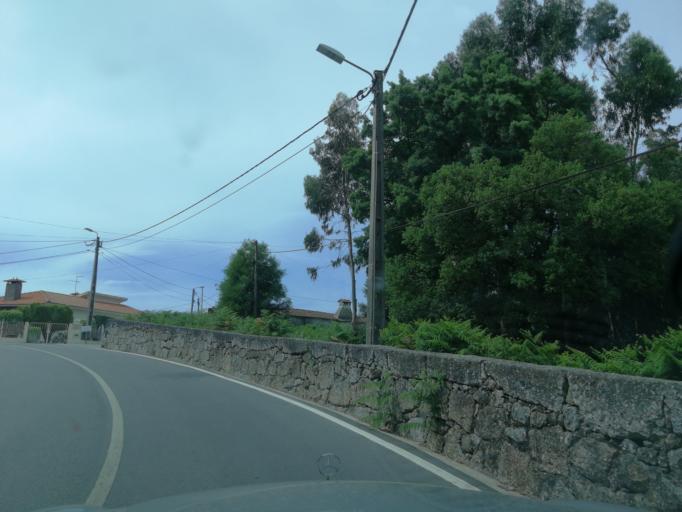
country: PT
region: Braga
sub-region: Vila Nova de Famalicao
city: Calendario
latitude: 41.4093
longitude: -8.5332
